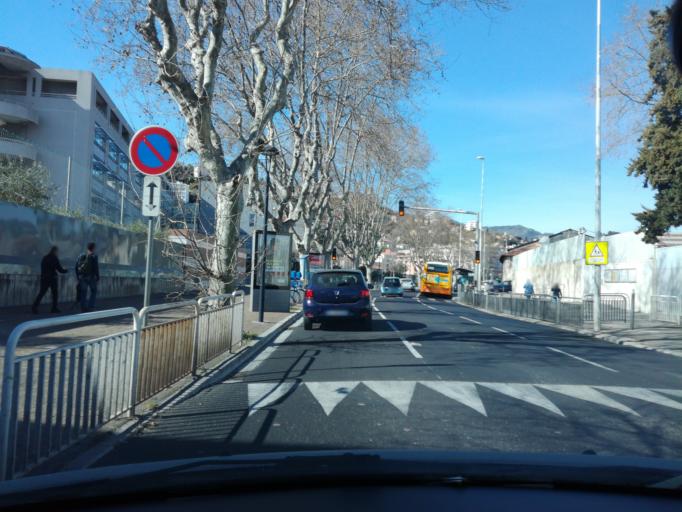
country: FR
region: Provence-Alpes-Cote d'Azur
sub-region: Departement des Alpes-Maritimes
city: Saint-Andre-de-la-Roche
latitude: 43.7147
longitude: 7.2831
